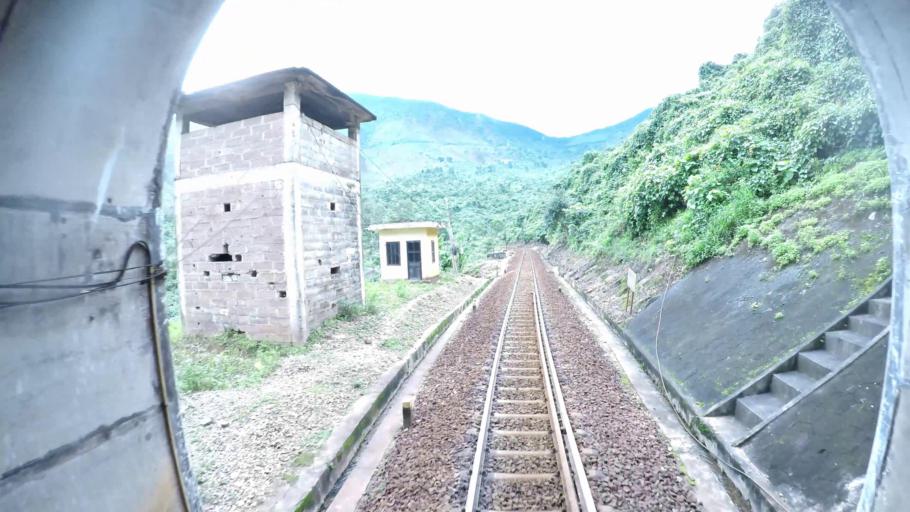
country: VN
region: Da Nang
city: Lien Chieu
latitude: 16.1738
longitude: 108.1388
